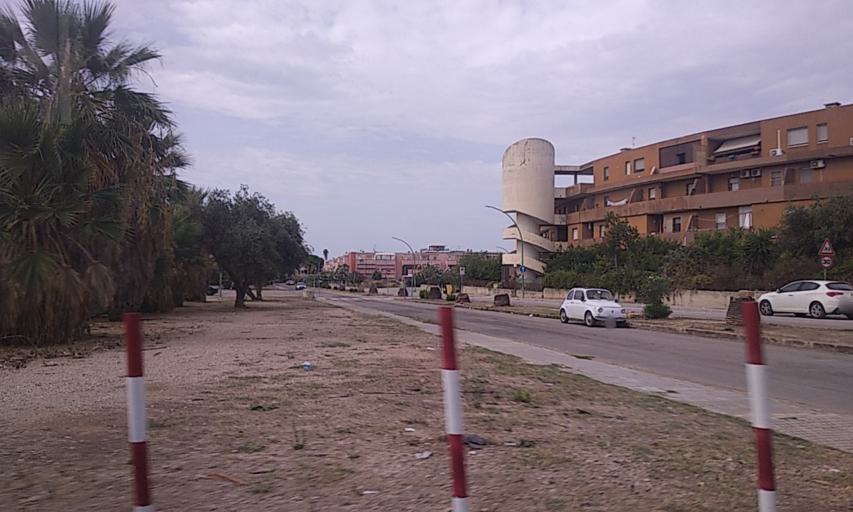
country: IT
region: Sardinia
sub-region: Provincia di Sassari
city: Alghero
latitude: 40.5788
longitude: 8.3190
